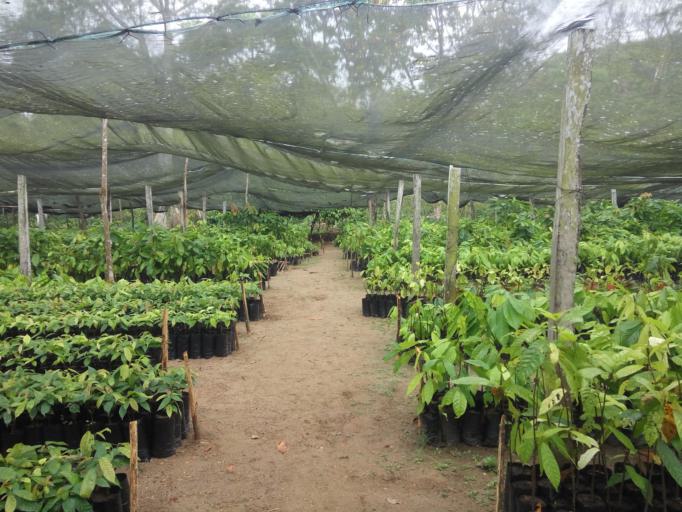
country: MX
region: Tabasco
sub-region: Comalcalco
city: Oriente 2da. Seccion (San Cayetano)
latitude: 18.1828
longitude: -93.2413
